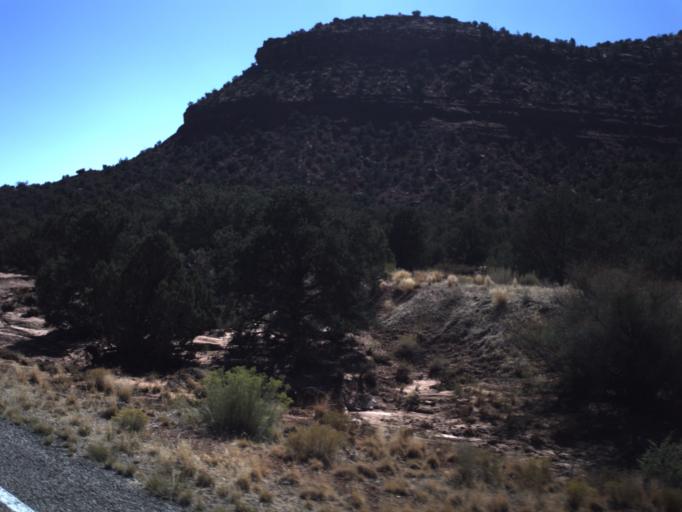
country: US
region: Utah
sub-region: San Juan County
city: Blanding
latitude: 37.6577
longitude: -110.1806
